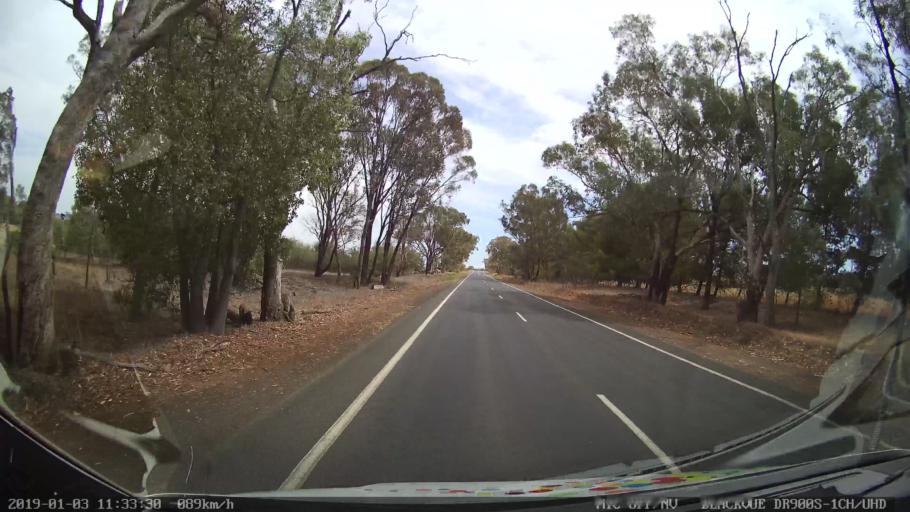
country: AU
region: New South Wales
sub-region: Weddin
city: Grenfell
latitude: -33.9461
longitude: 148.1704
